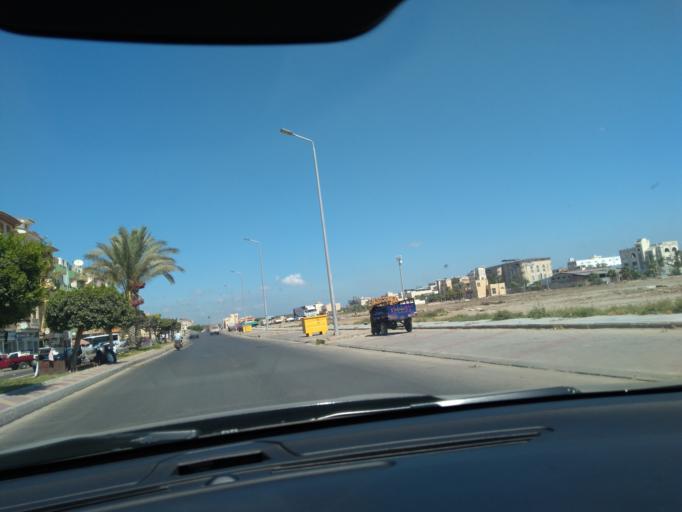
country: EG
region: Dumyat
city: Faraskur
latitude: 31.4260
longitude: 31.6810
